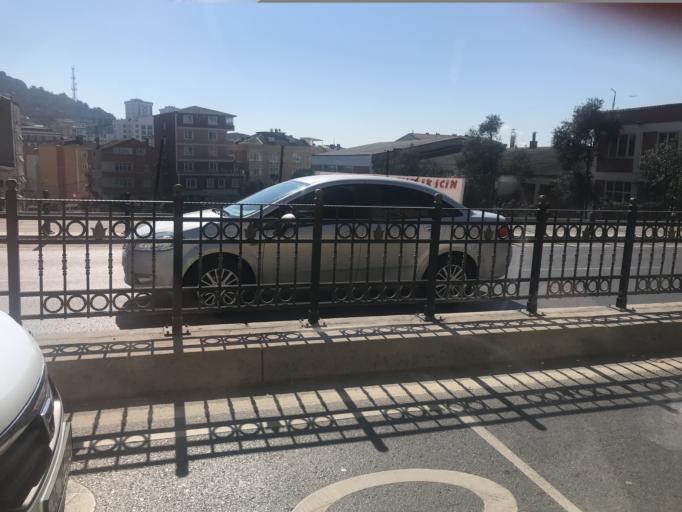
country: TR
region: Istanbul
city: Pendik
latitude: 40.8954
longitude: 29.2479
